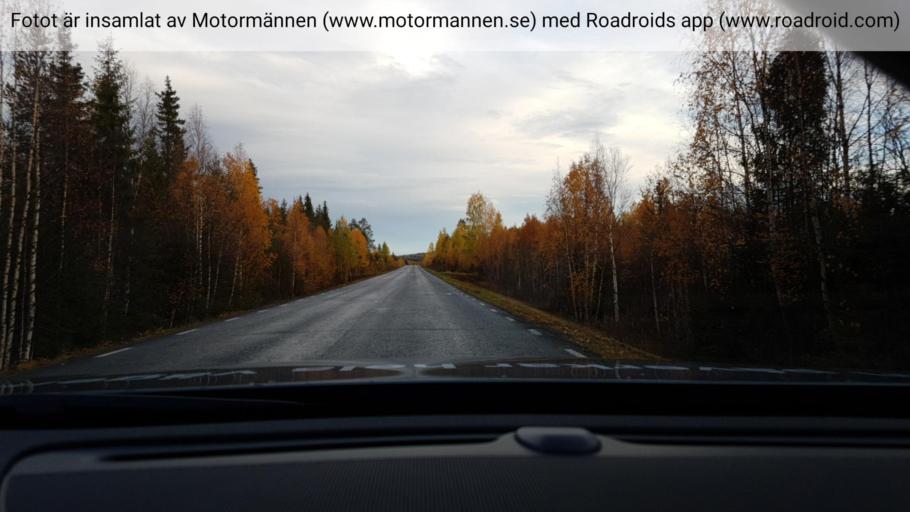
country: SE
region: Norrbotten
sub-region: Overkalix Kommun
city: OEverkalix
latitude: 66.9188
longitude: 22.7547
